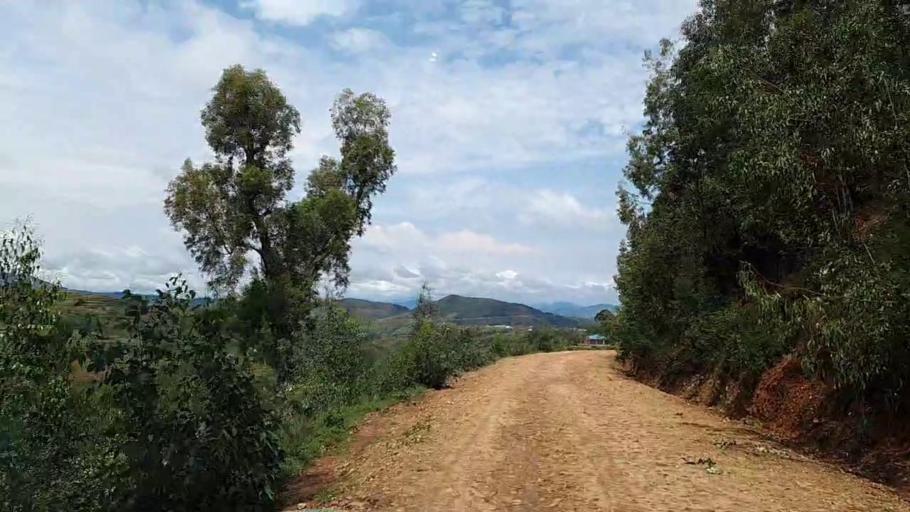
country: RW
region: Southern Province
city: Gikongoro
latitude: -2.3382
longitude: 29.5175
